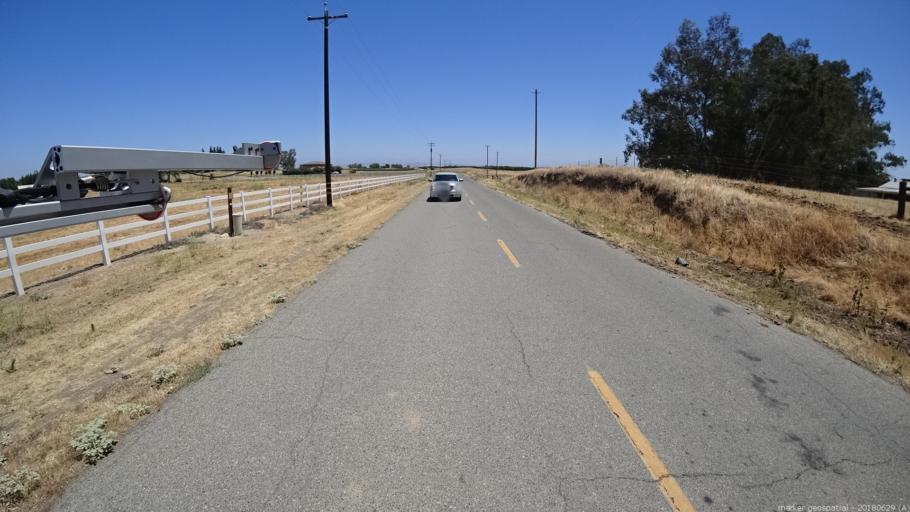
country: US
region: California
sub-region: Madera County
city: Parksdale
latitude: 37.0054
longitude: -119.9785
